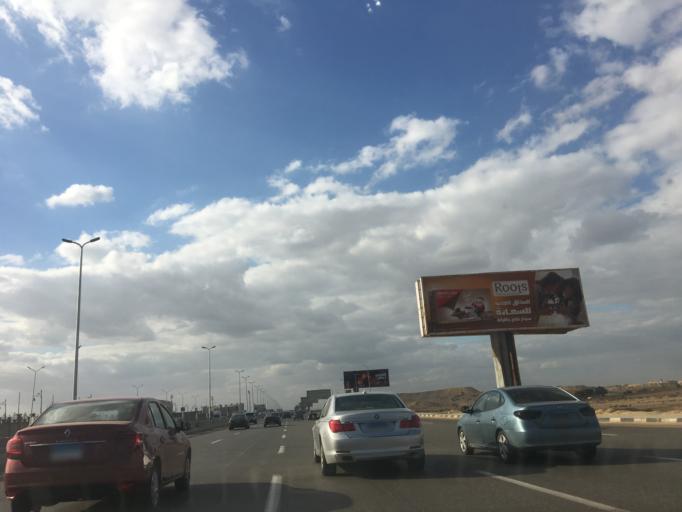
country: EG
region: Muhafazat al Qahirah
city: Cairo
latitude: 30.0185
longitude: 31.3865
